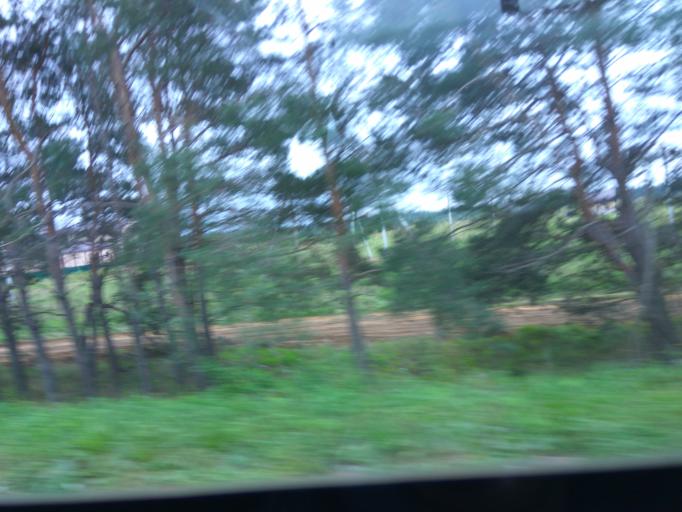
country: RU
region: Moskovskaya
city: Malyshevo
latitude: 55.5293
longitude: 38.3378
